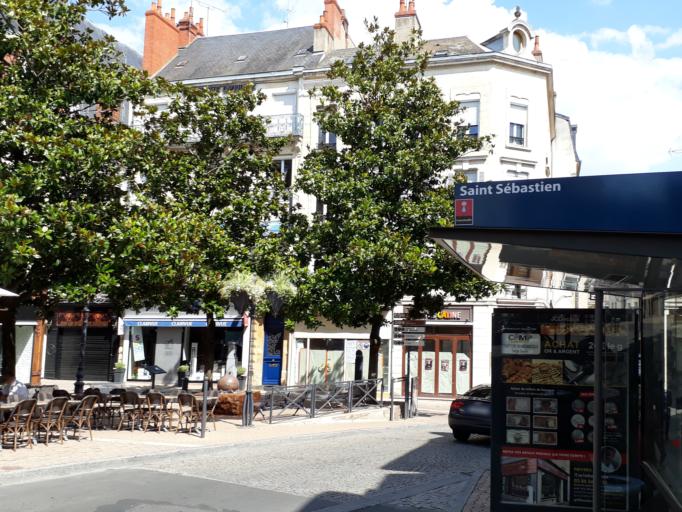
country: FR
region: Bourgogne
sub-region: Departement de la Nievre
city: Nevers
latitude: 46.9894
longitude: 3.1616
